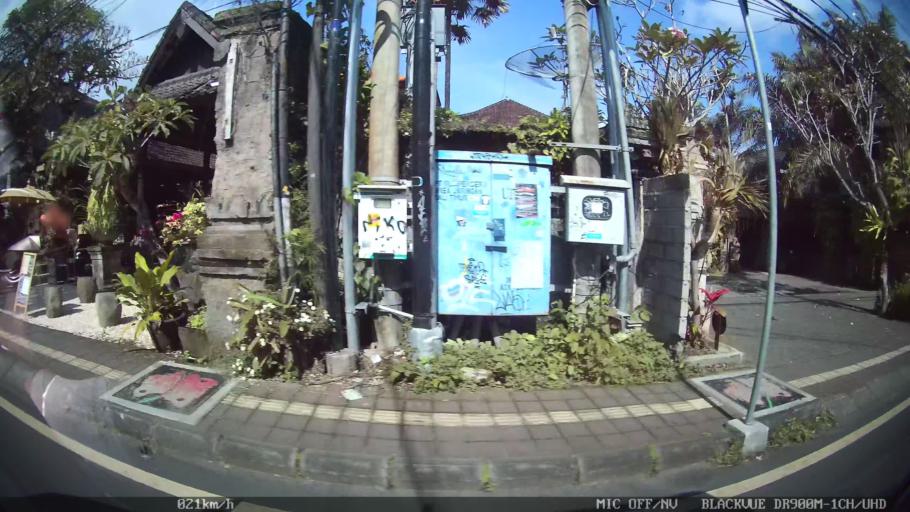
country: ID
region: Bali
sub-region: Kabupaten Gianyar
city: Ubud
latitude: -8.5159
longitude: 115.2603
